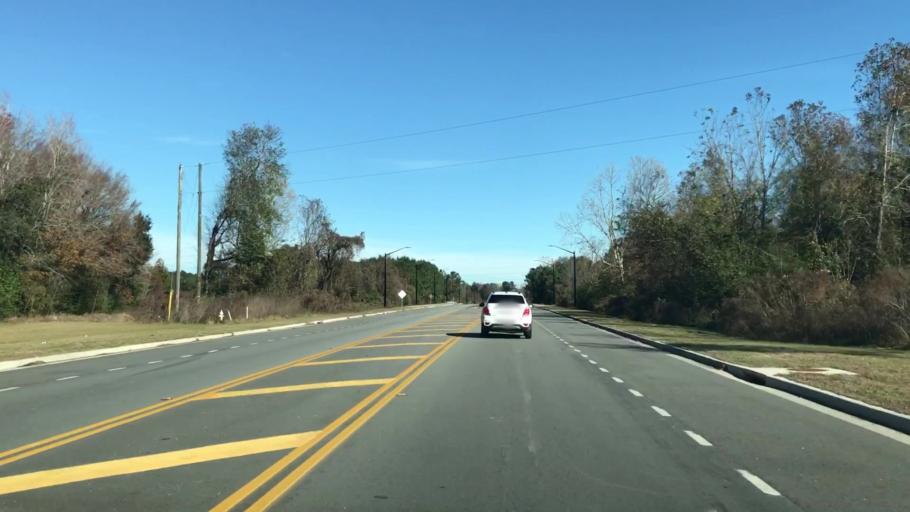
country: US
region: South Carolina
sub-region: Dorchester County
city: Summerville
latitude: 33.0399
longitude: -80.1838
